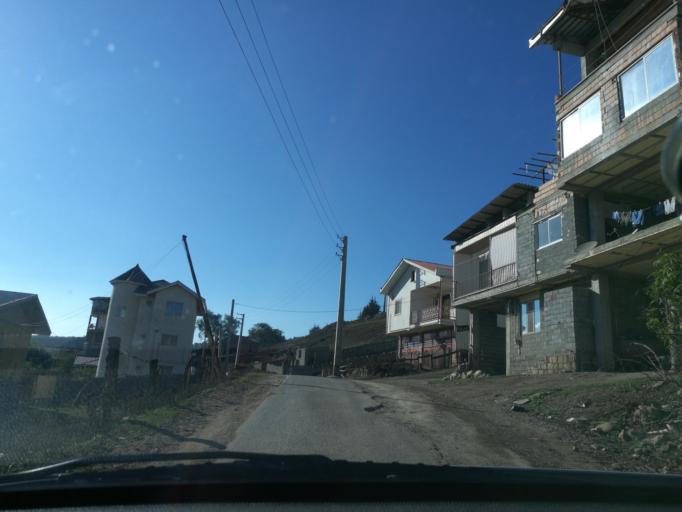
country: IR
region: Mazandaran
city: `Abbasabad
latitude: 36.5575
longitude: 51.1915
